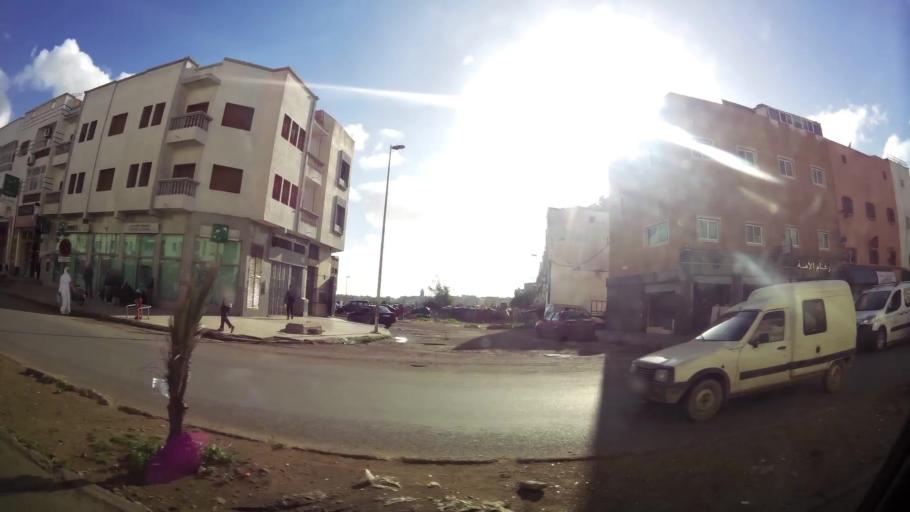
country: MA
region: Grand Casablanca
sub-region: Casablanca
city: Casablanca
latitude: 33.5674
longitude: -7.6844
